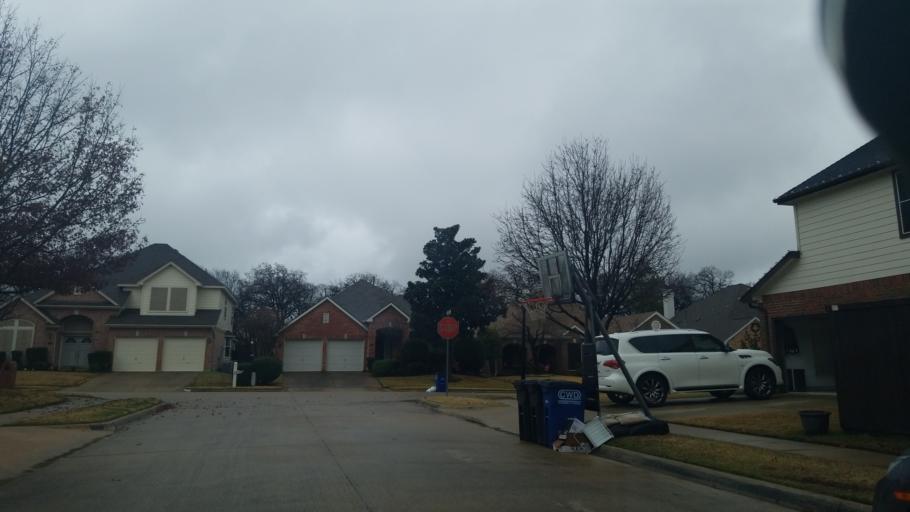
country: US
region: Texas
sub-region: Denton County
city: Corinth
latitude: 33.1533
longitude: -97.0846
